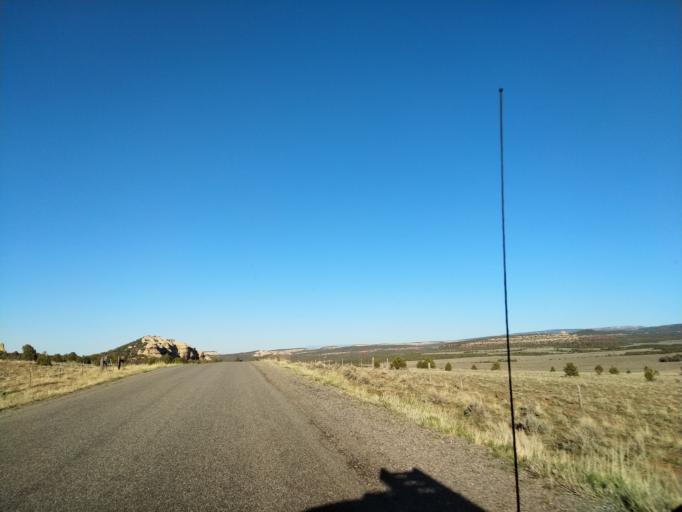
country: US
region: Colorado
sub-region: Mesa County
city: Loma
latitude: 38.9512
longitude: -108.9546
